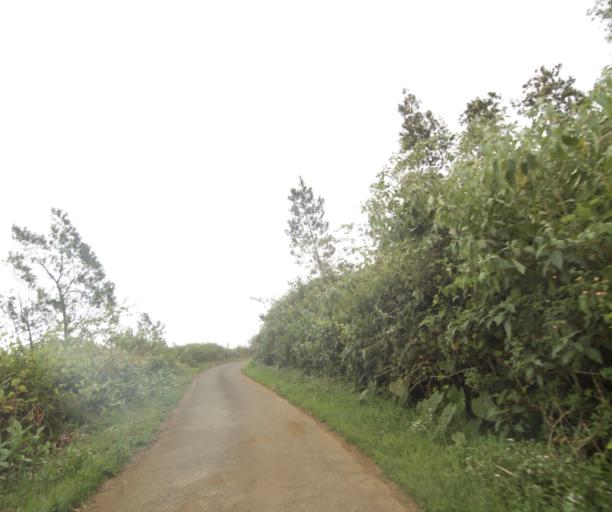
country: RE
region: Reunion
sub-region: Reunion
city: Saint-Paul
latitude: -21.0148
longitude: 55.3508
